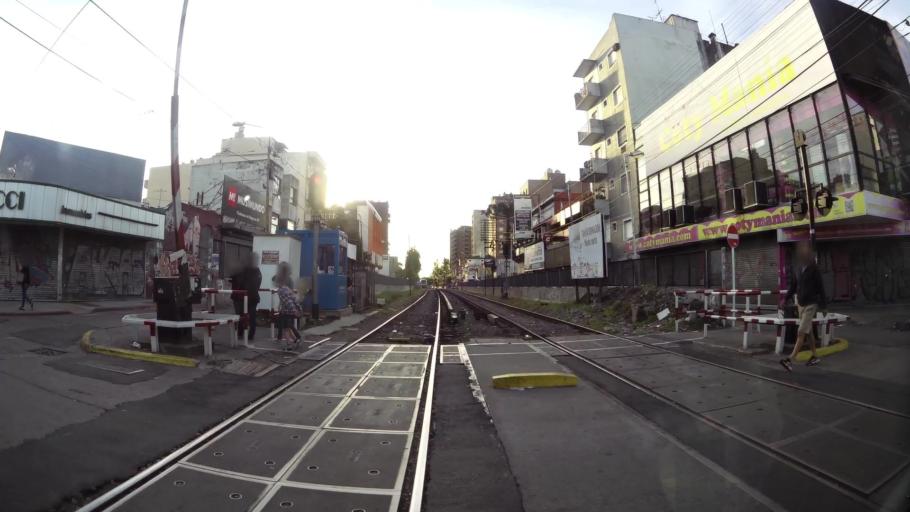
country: AR
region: Buenos Aires
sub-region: Partido de Moron
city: Moron
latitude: -34.6482
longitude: -58.6211
